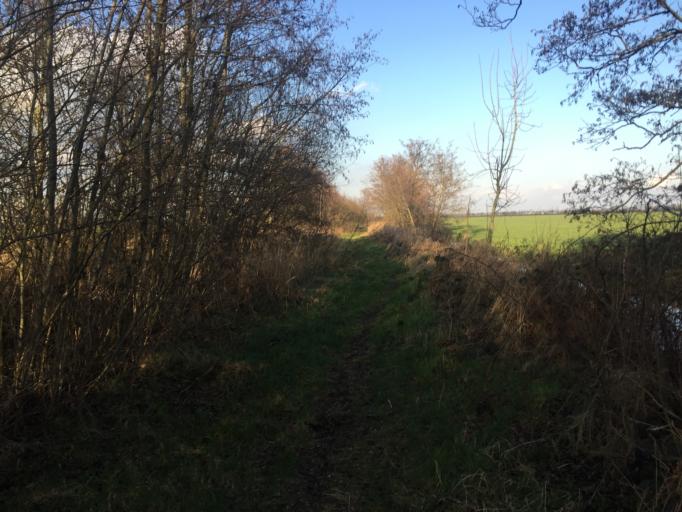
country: NL
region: Utrecht
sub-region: Gemeente Oudewater
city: Oudewater
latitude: 52.0397
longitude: 4.8202
